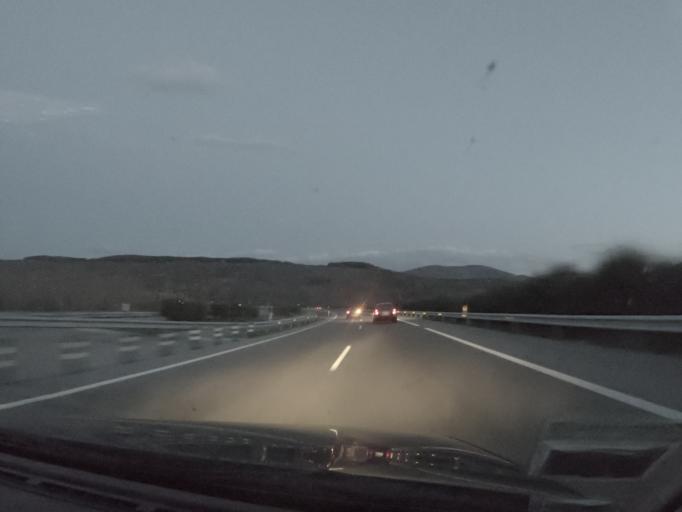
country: ES
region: Castille and Leon
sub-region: Provincia de Leon
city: Torre del Bierzo
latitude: 42.6056
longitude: -6.3841
